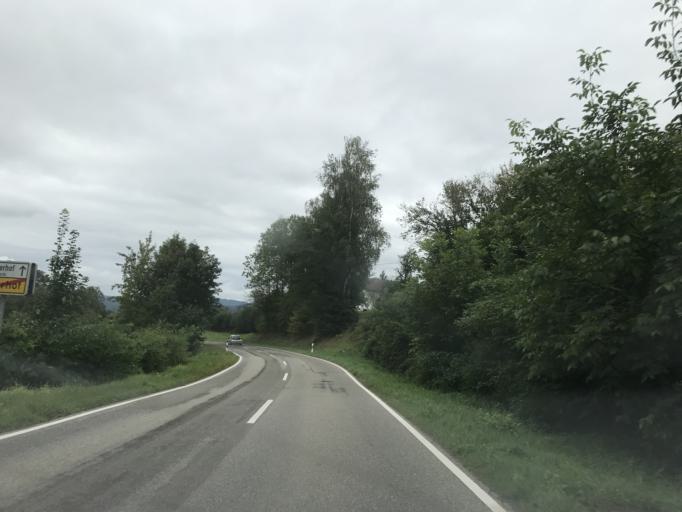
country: DE
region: Baden-Wuerttemberg
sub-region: Freiburg Region
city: Murg
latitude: 47.5815
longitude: 8.0331
